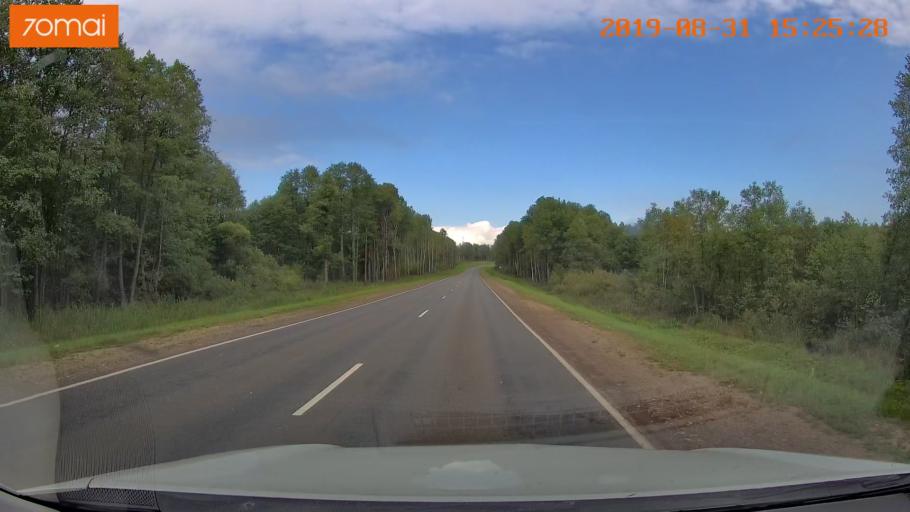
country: RU
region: Kaluga
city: Baryatino
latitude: 54.5419
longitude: 34.5202
